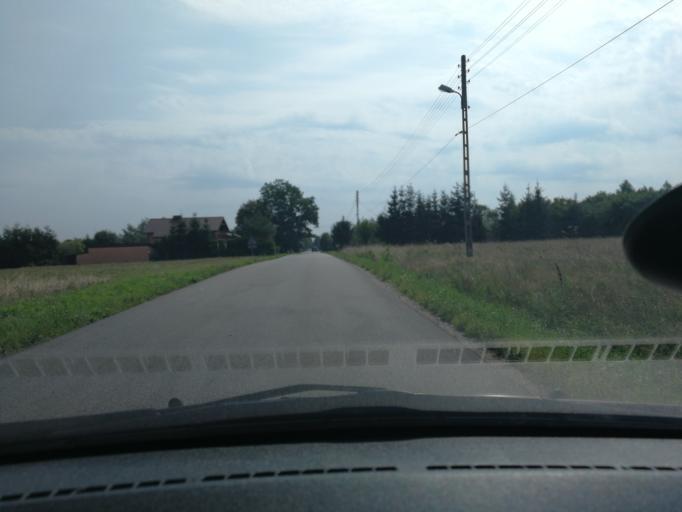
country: PL
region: Lodz Voivodeship
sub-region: Powiat skierniewicki
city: Makow
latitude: 51.9933
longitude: 20.0804
